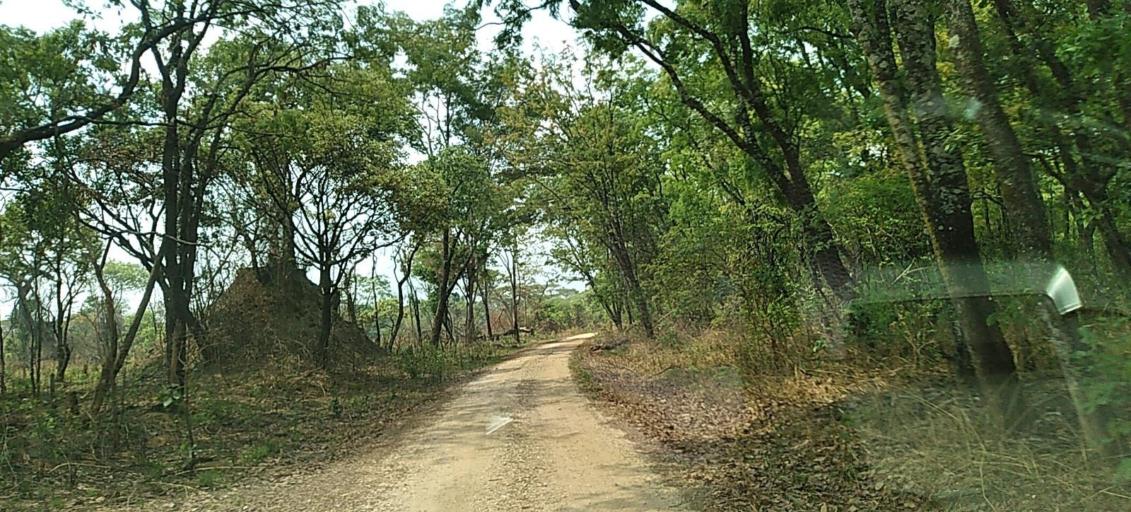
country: ZM
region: Copperbelt
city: Chingola
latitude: -12.7457
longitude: 27.7249
